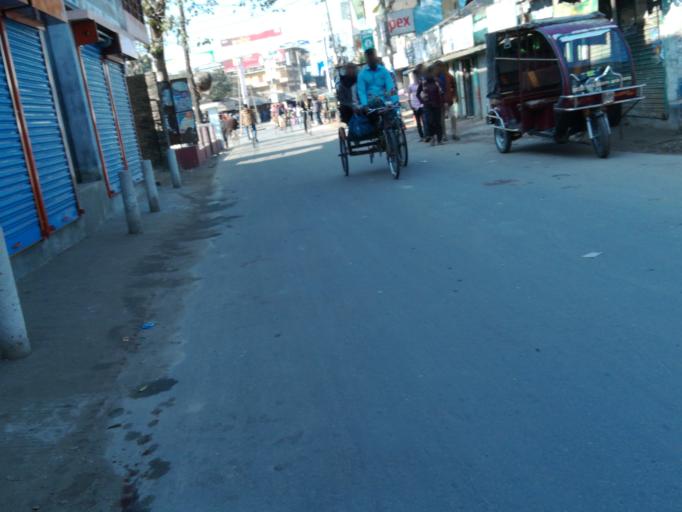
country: BD
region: Rangpur Division
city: Nageswari
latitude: 25.8131
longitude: 89.6452
